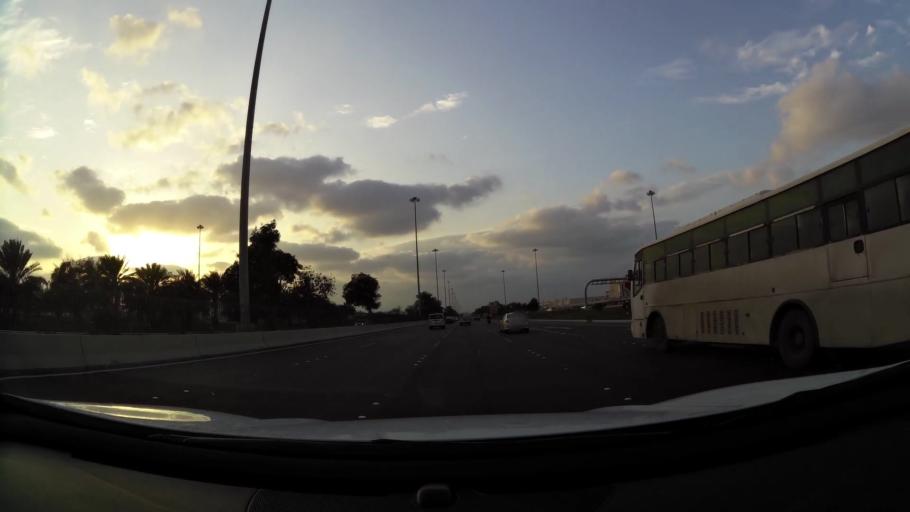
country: AE
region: Abu Dhabi
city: Abu Dhabi
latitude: 24.4155
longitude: 54.5021
